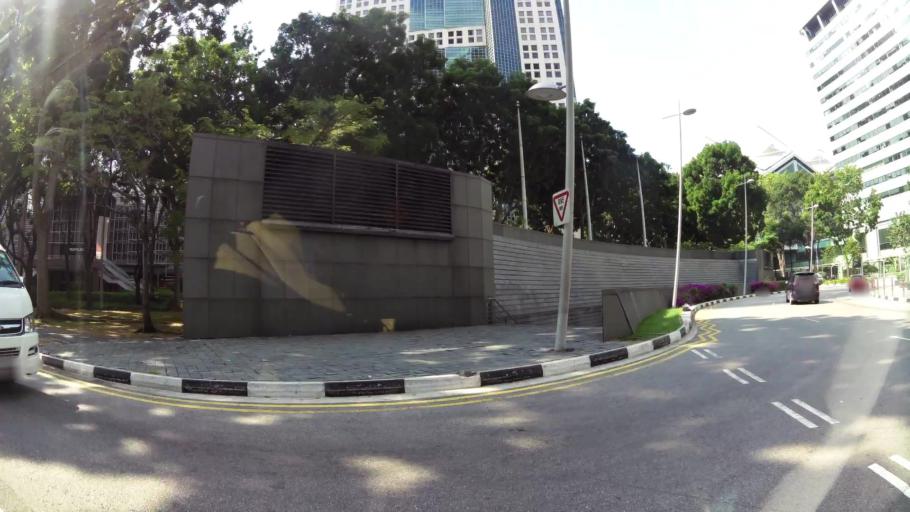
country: SG
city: Singapore
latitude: 1.2931
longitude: 103.8588
